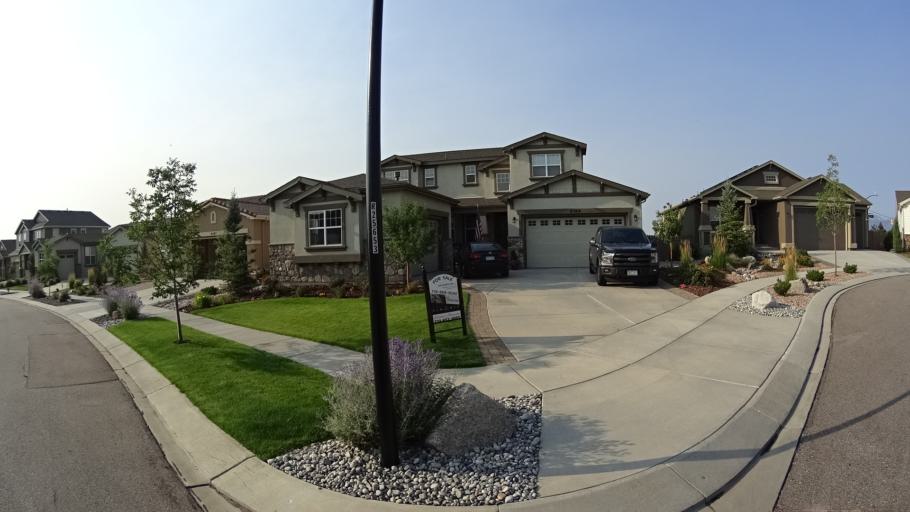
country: US
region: Colorado
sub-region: El Paso County
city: Black Forest
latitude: 38.9719
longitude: -104.7311
